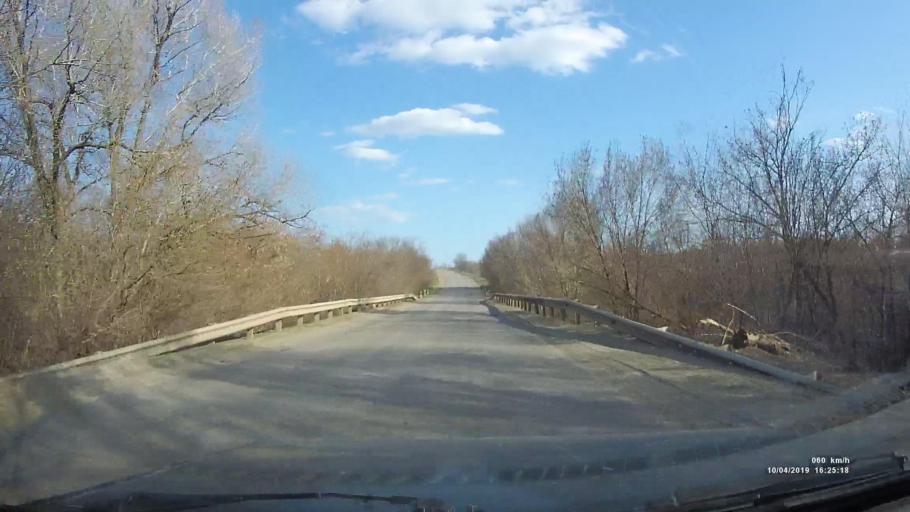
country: RU
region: Rostov
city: Staraya Stanitsa
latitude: 48.2937
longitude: 40.3223
